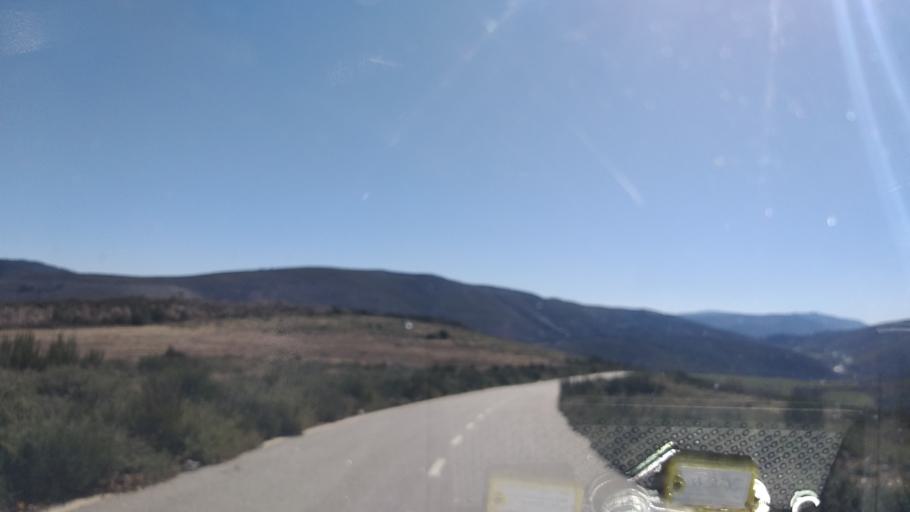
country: PT
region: Guarda
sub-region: Manteigas
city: Manteigas
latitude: 40.4690
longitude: -7.5026
